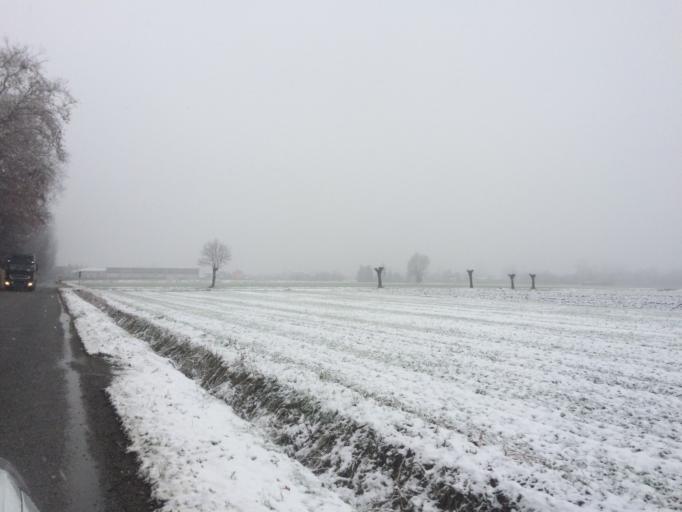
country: IT
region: Piedmont
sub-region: Provincia di Cuneo
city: Racconigi
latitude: 44.7743
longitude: 7.6704
